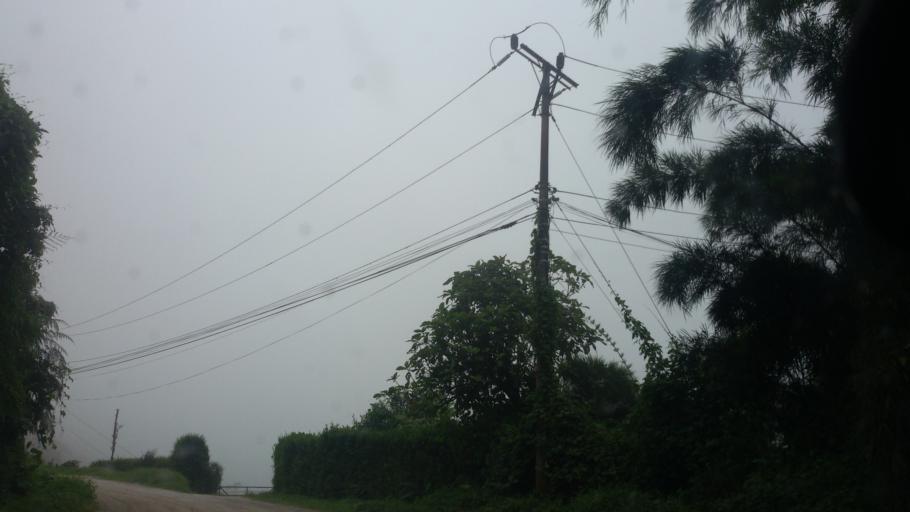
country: CR
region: San Jose
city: Ipis
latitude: 10.0210
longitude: -83.9478
